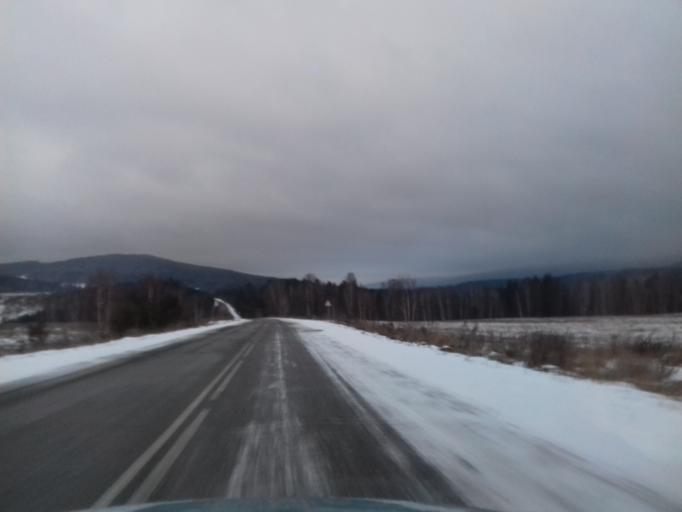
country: RU
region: Bashkortostan
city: Verkhniy Avzyan
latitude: 53.7644
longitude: 57.9323
